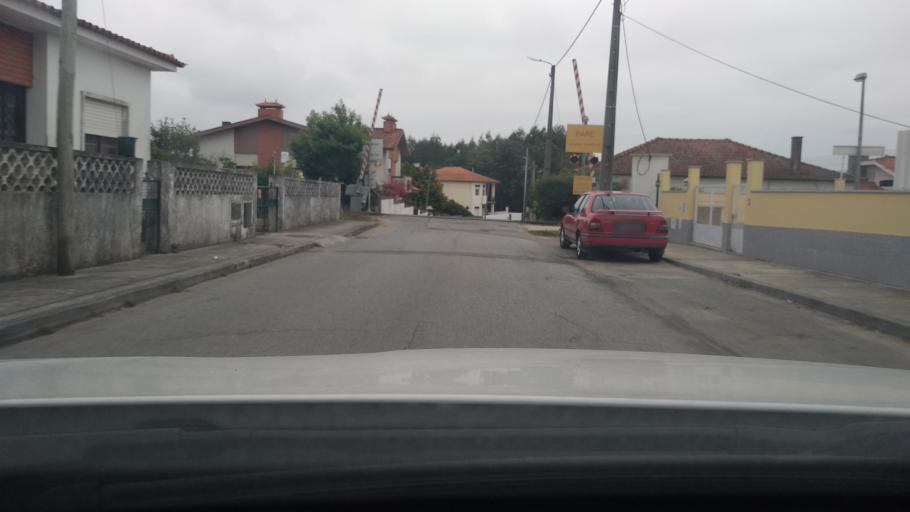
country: PT
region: Aveiro
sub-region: Espinho
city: Souto
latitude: 40.9824
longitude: -8.6250
